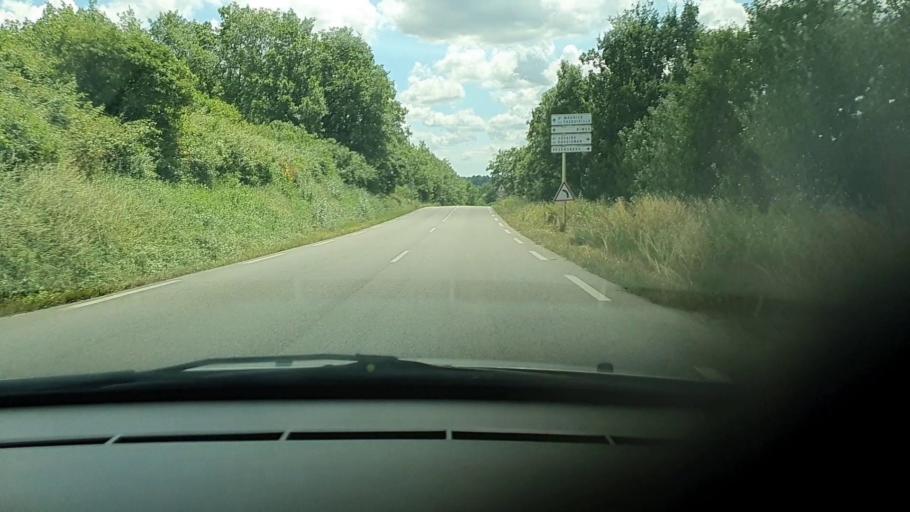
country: FR
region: Languedoc-Roussillon
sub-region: Departement du Gard
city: Moussac
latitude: 44.0389
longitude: 4.2322
